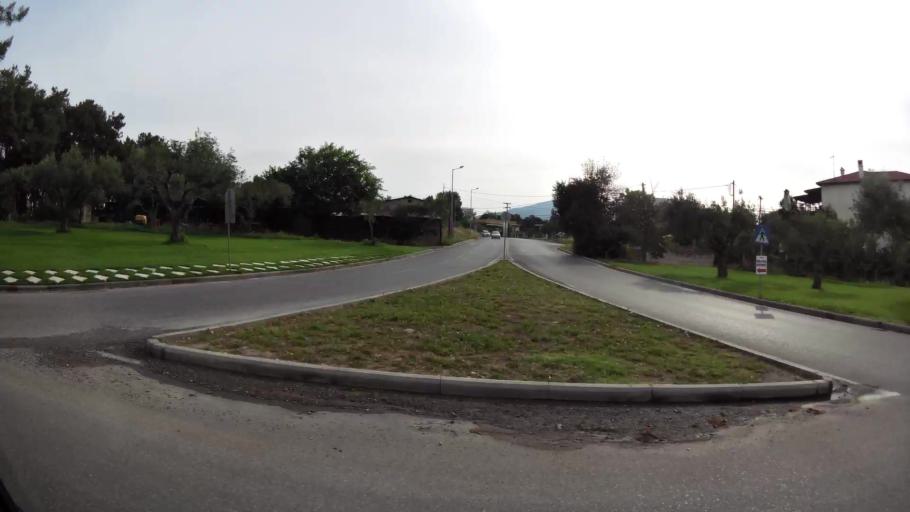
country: GR
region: Central Macedonia
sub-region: Nomos Thessalonikis
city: Thermi
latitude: 40.5530
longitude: 23.0173
